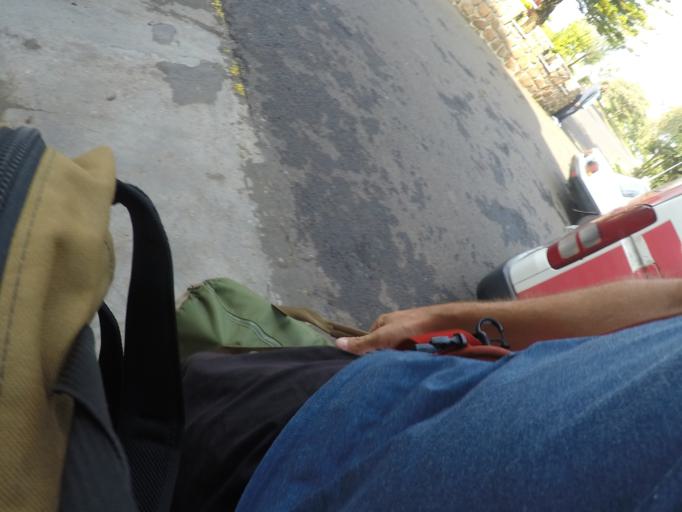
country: ET
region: Amhara
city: Gondar
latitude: 12.5165
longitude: 37.4307
